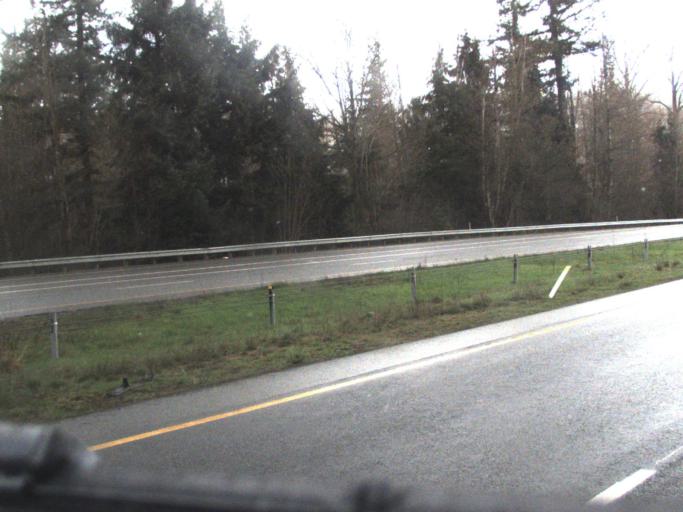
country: US
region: Washington
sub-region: King County
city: Hobart
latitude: 47.4336
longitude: -121.9809
